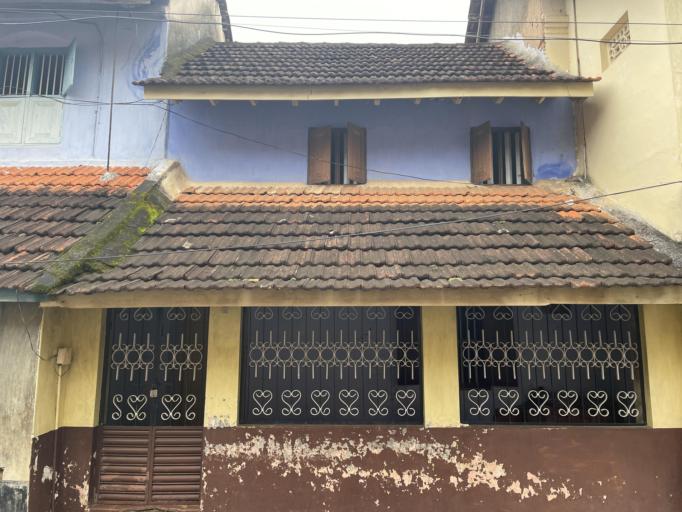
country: IN
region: Kerala
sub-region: Palakkad district
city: Chittur
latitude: 10.6933
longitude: 76.7401
